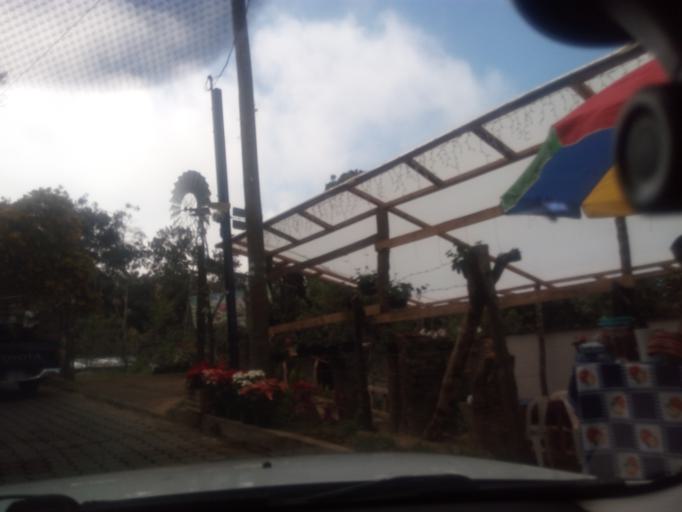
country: GT
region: Sacatepequez
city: San Bartolome Milpas Altas
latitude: 14.5988
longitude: -90.6811
